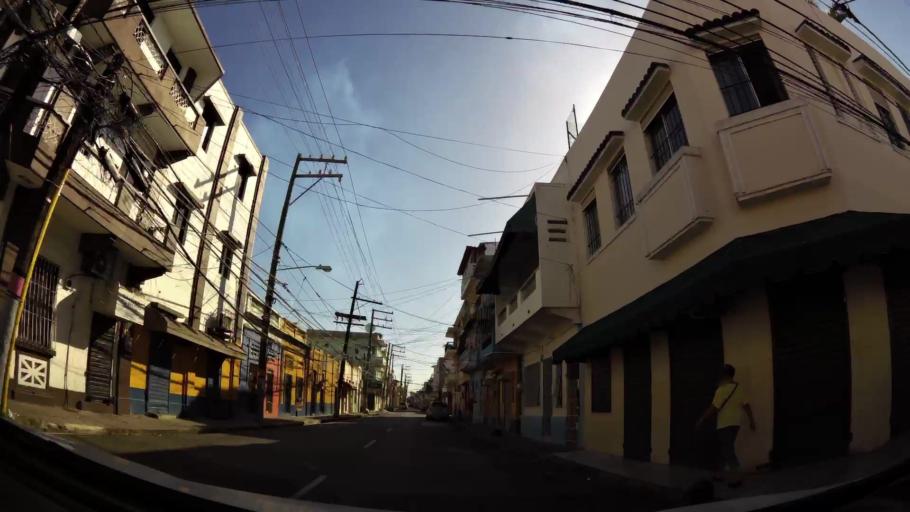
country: DO
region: Nacional
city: Ciudad Nueva
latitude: 18.4692
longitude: -69.8915
